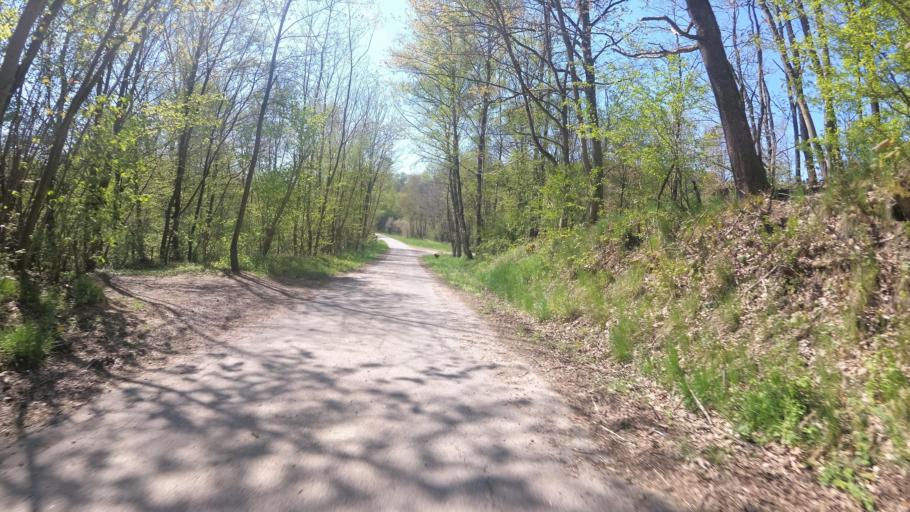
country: DE
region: Saarland
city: Marpingen
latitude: 49.4804
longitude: 7.0740
